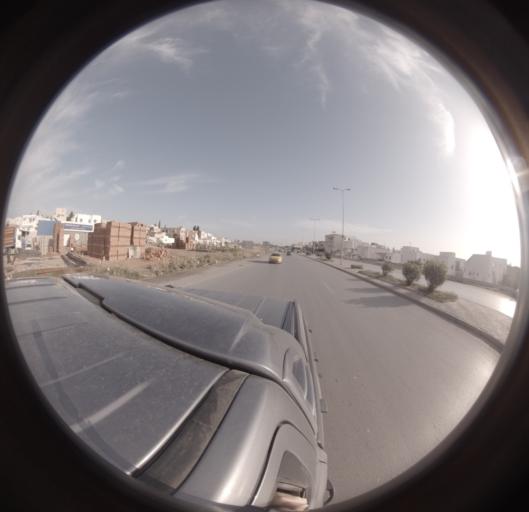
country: TN
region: Zaghwan
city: El Fahs
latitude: 36.4533
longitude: 9.9631
